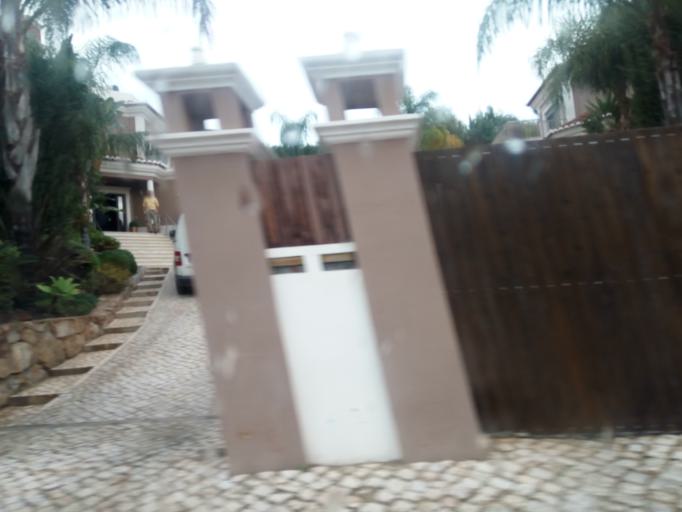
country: PT
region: Faro
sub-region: Faro
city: Santa Barbara de Nexe
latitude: 37.1057
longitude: -7.9789
